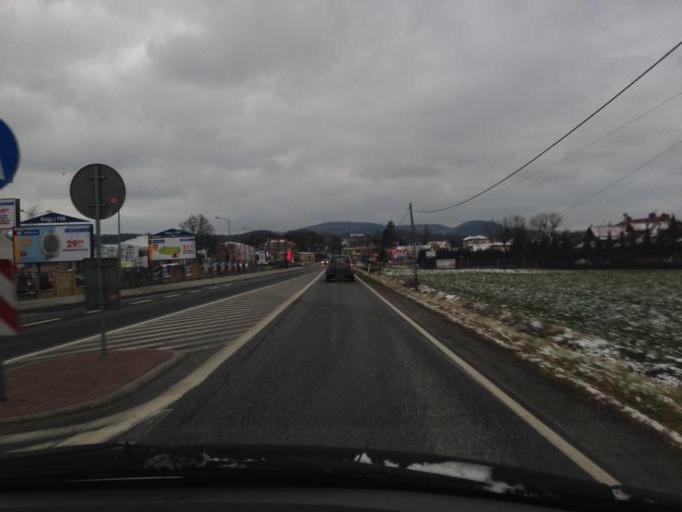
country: PL
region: Lesser Poland Voivodeship
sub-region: Powiat tarnowski
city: Zakliczyn
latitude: 49.8604
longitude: 20.8137
